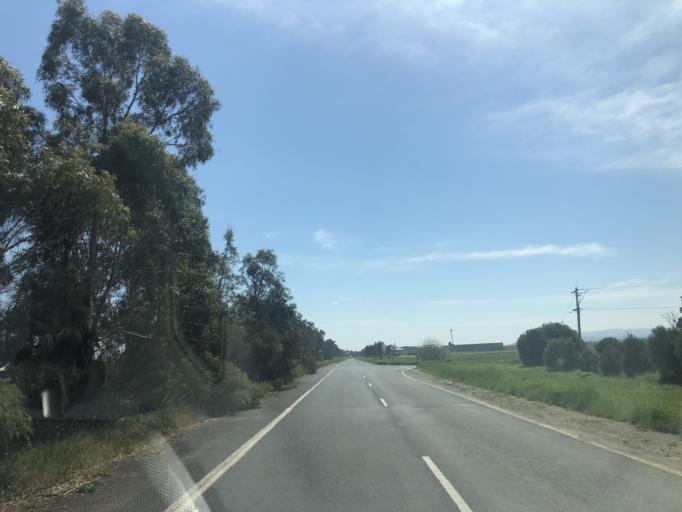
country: AU
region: Victoria
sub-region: Frankston
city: Sandhurst
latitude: -38.0565
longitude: 145.1848
